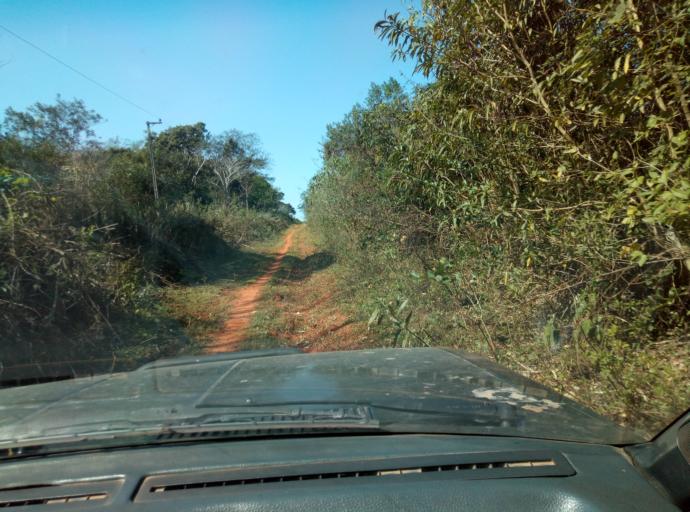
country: PY
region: Caaguazu
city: Doctor Cecilio Baez
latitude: -25.1793
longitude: -56.2144
